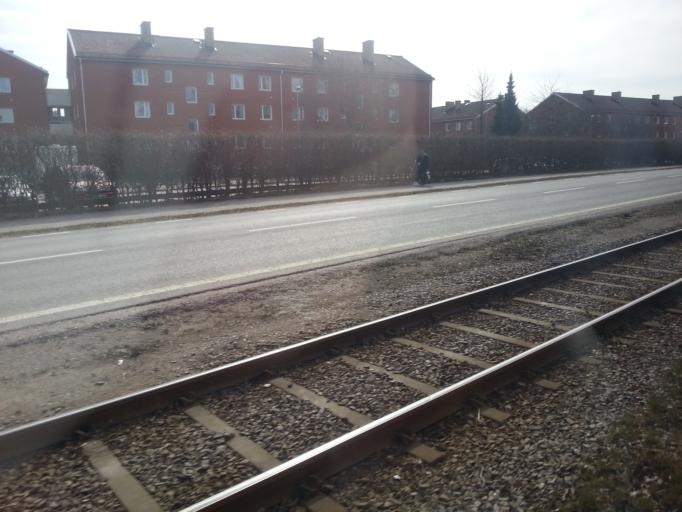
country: SE
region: OEstergoetland
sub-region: Norrkopings Kommun
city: Norrkoping
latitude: 58.5790
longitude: 16.1534
